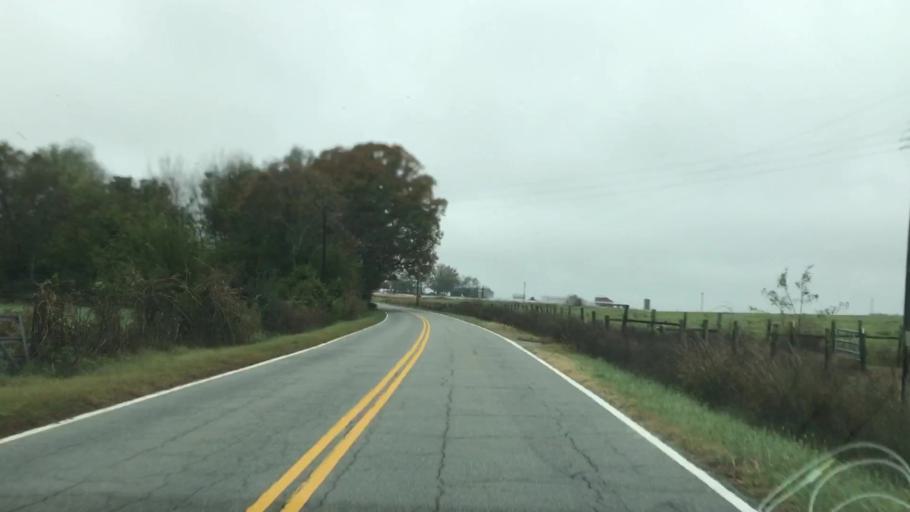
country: US
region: South Carolina
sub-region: Laurens County
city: Joanna
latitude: 34.3566
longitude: -81.7984
